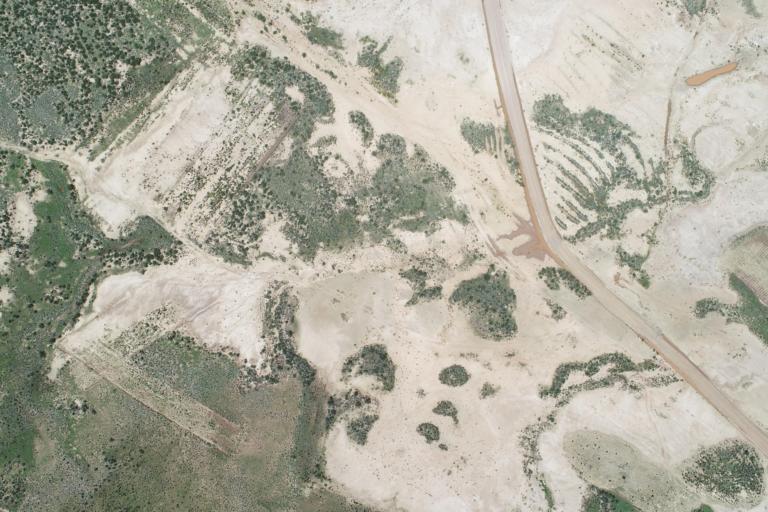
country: BO
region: La Paz
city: Curahuara de Carangas
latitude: -17.3169
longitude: -68.4985
